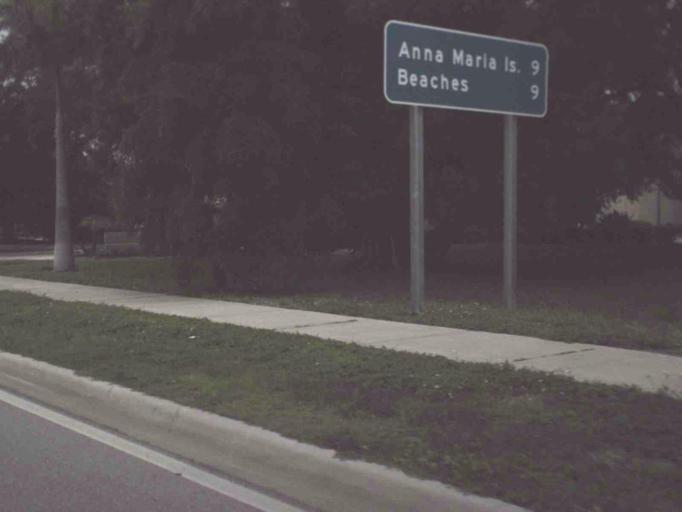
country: US
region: Florida
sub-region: Manatee County
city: Bradenton
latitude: 27.4953
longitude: -82.5638
